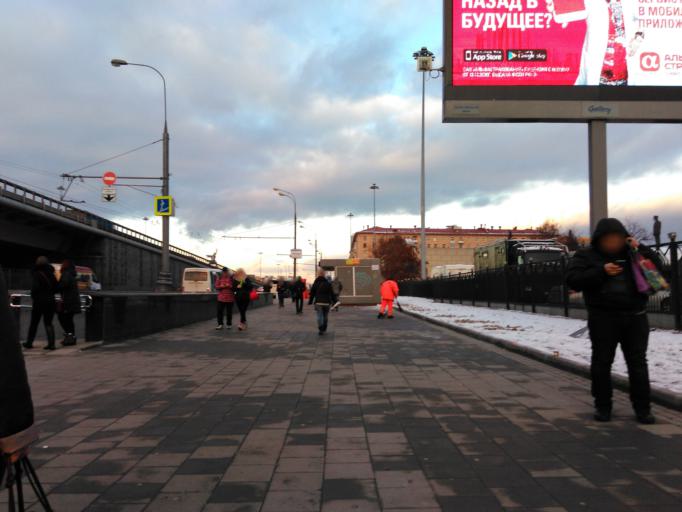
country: RU
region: Moscow
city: Rostokino
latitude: 55.8220
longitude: 37.6433
